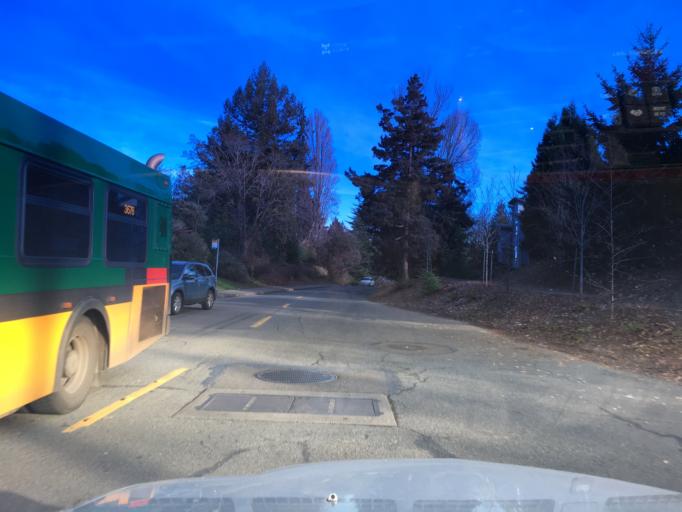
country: US
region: Washington
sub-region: King County
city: Yarrow Point
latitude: 47.6757
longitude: -122.2633
